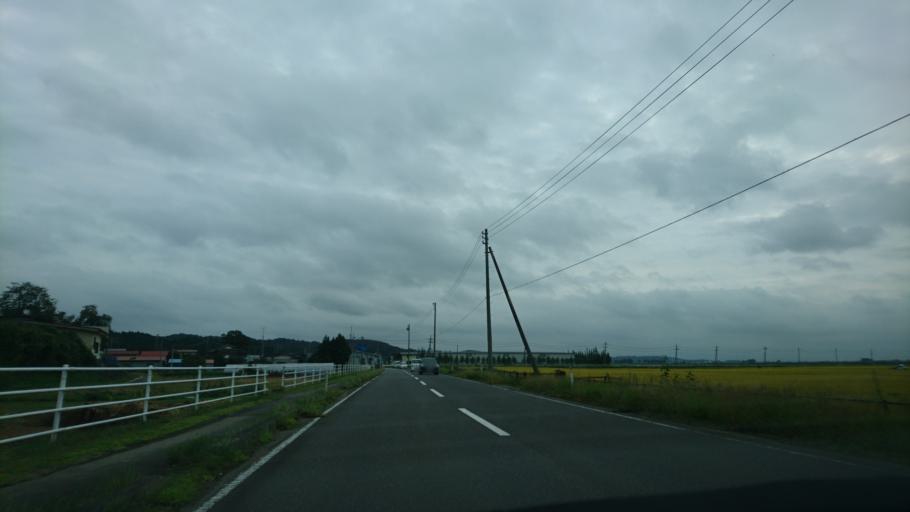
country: JP
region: Iwate
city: Ichinoseki
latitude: 38.8014
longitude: 141.1190
